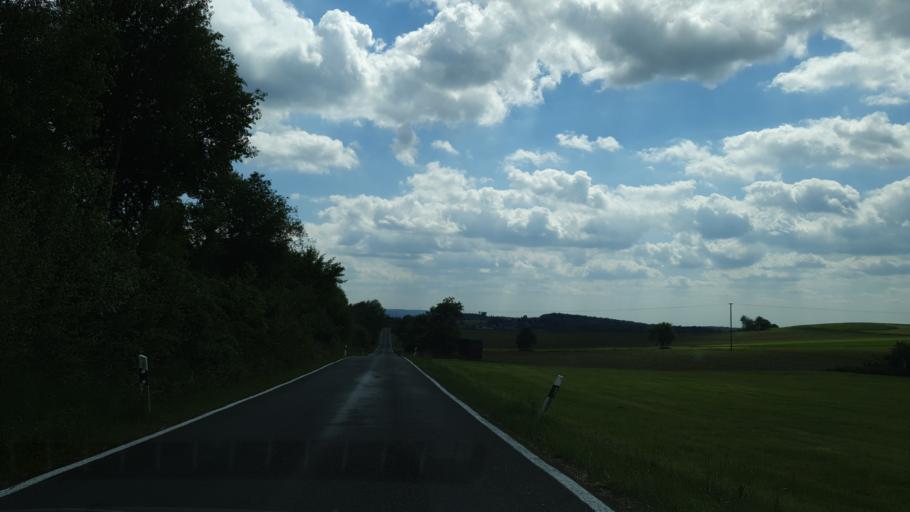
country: DE
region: Rheinland-Pfalz
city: Weidenhahn
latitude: 50.5530
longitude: 7.8460
